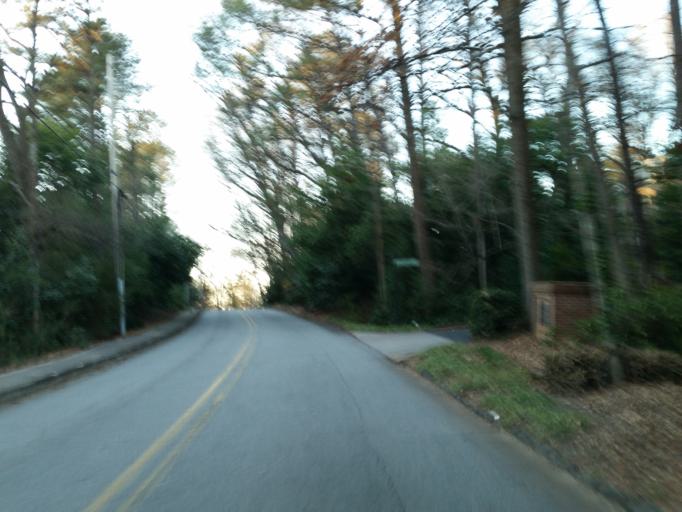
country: US
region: Georgia
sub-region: Cobb County
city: Vinings
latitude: 33.8154
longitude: -84.4284
